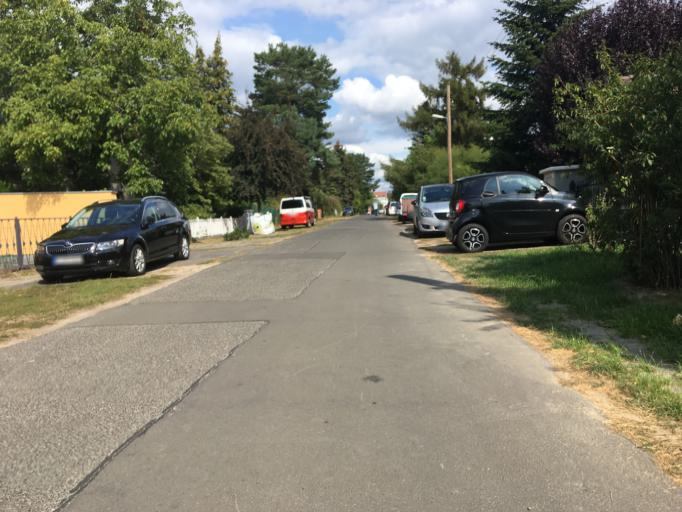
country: DE
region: Berlin
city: Karow
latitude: 52.6102
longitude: 13.4897
